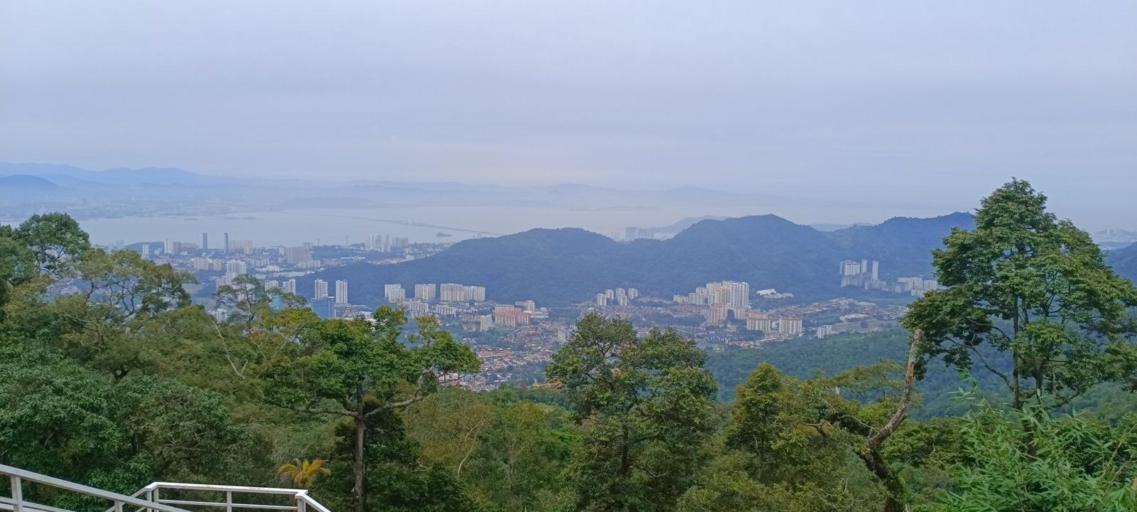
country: MY
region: Penang
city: Tanjung Tokong
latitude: 5.4113
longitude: 100.2611
